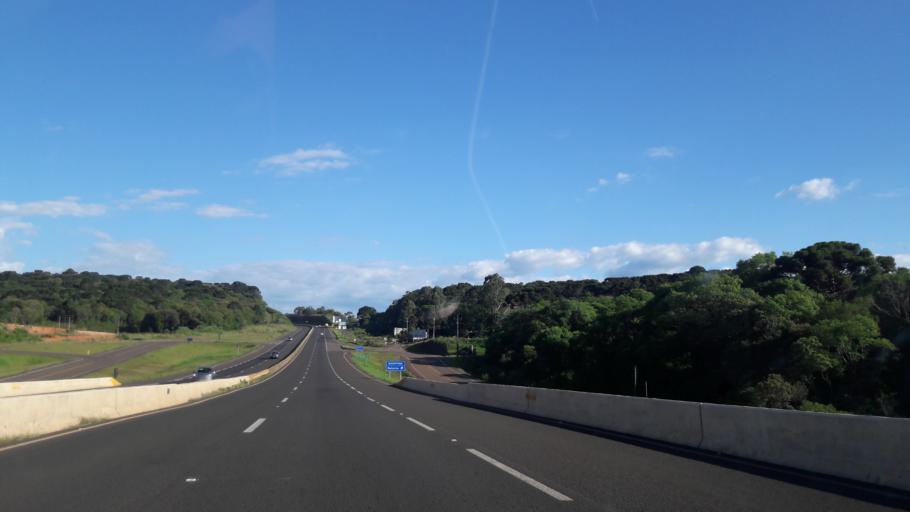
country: BR
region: Parana
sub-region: Guarapuava
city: Guarapuava
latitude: -25.3415
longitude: -51.4130
